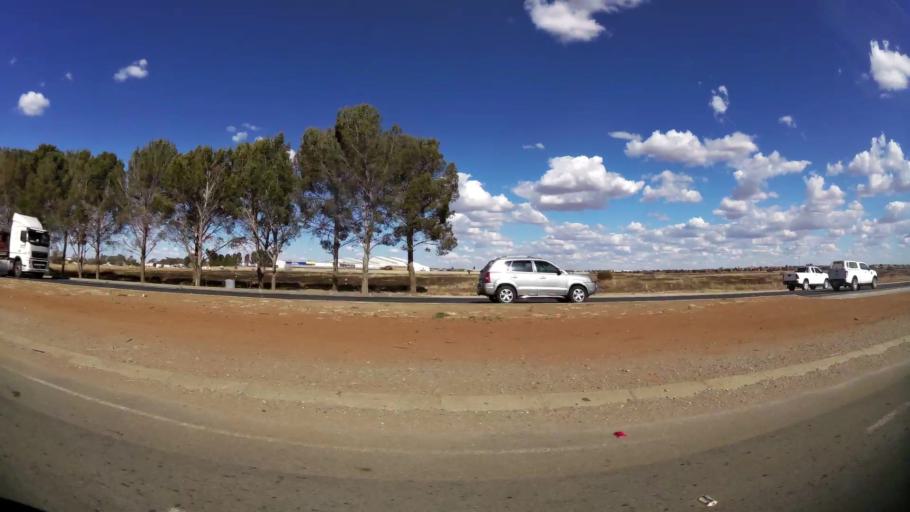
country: ZA
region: North-West
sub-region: Dr Kenneth Kaunda District Municipality
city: Klerksdorp
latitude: -26.8701
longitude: 26.6185
